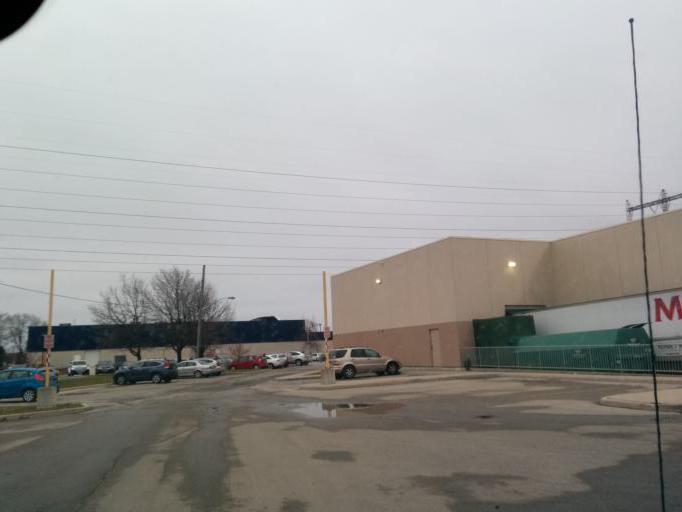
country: CA
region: Ontario
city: Etobicoke
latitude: 43.6167
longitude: -79.5600
